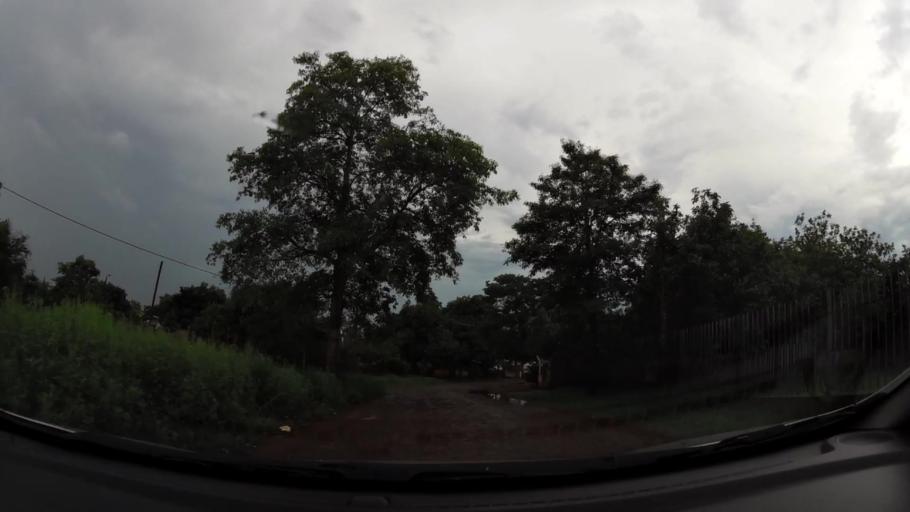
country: PY
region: Alto Parana
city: Presidente Franco
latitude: -25.5480
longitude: -54.6519
